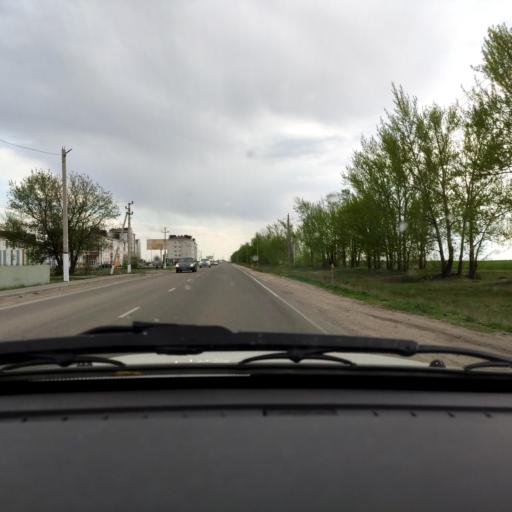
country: RU
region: Voronezj
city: Novaya Usman'
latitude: 51.6052
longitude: 39.3733
